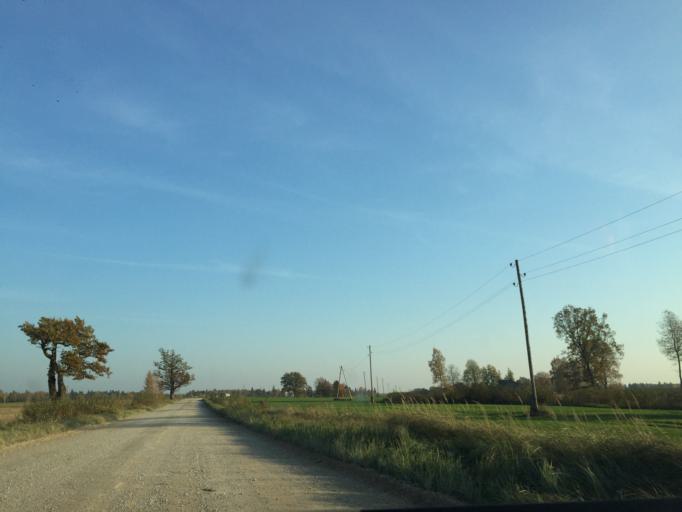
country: LV
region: Vainode
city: Vainode
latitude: 56.6109
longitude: 21.8190
